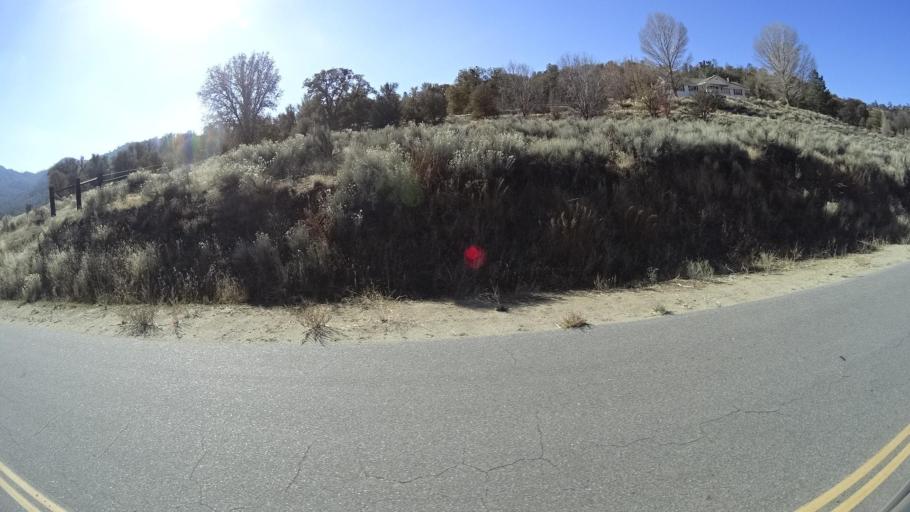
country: US
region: California
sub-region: Kern County
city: Bodfish
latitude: 35.3825
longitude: -118.5502
